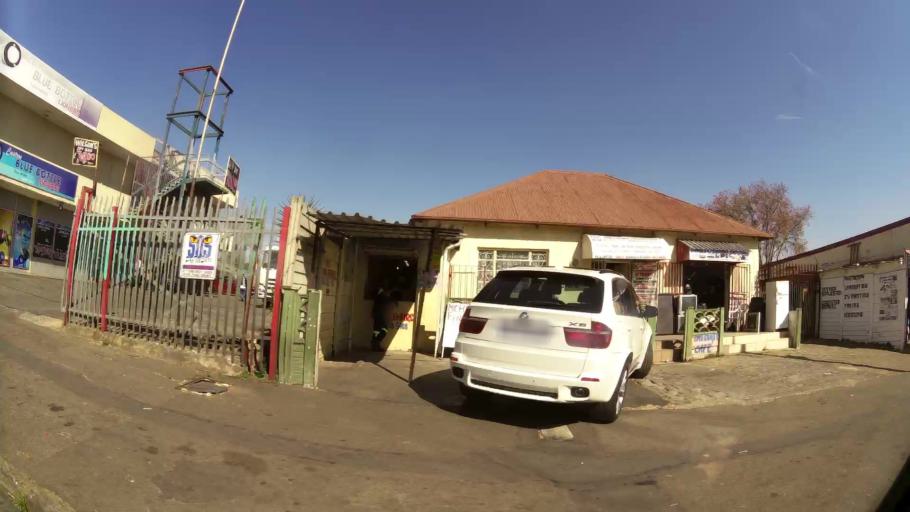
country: ZA
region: Gauteng
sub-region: City of Johannesburg Metropolitan Municipality
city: Johannesburg
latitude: -26.2387
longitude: 28.0305
